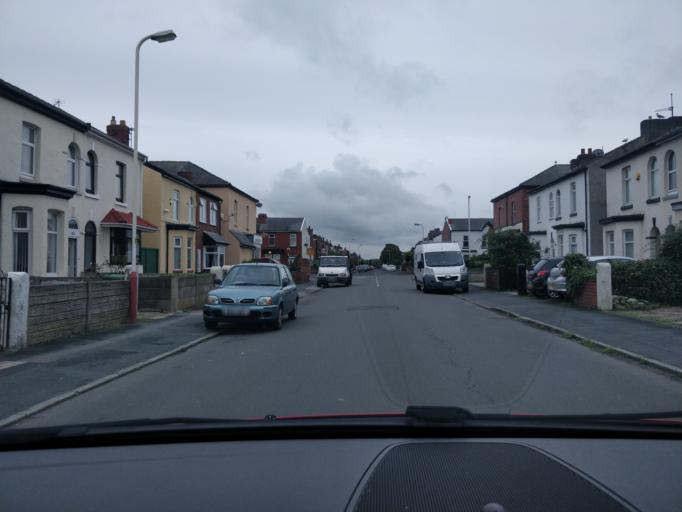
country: GB
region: England
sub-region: Sefton
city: Southport
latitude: 53.6345
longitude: -3.0030
